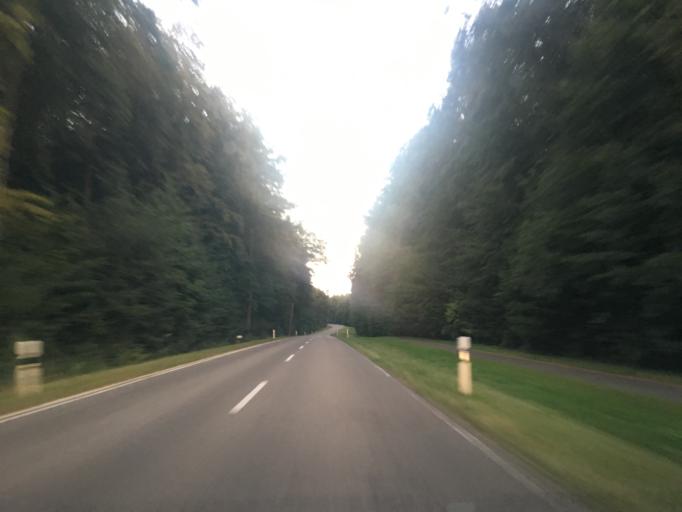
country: DE
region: Baden-Wuerttemberg
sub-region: Tuebingen Region
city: Hayingen
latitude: 48.3040
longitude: 9.4490
